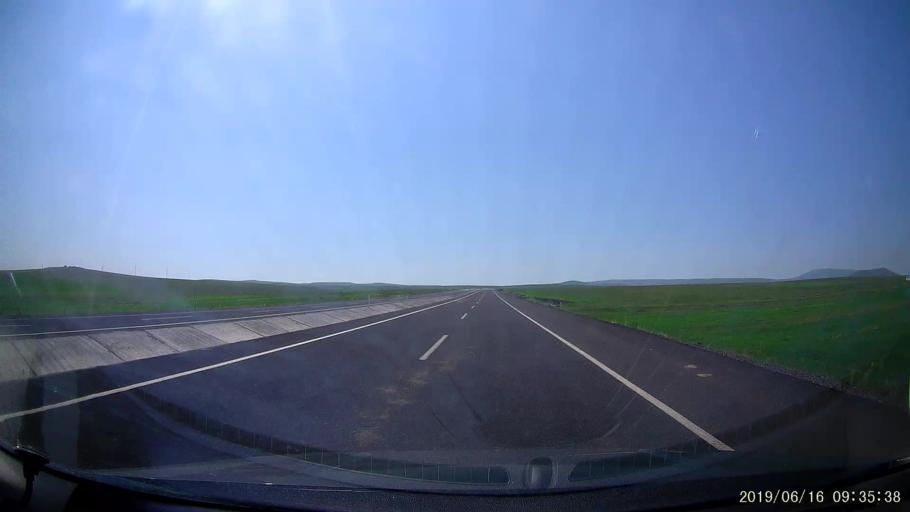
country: TR
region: Kars
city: Kars
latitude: 40.5688
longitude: 43.1591
